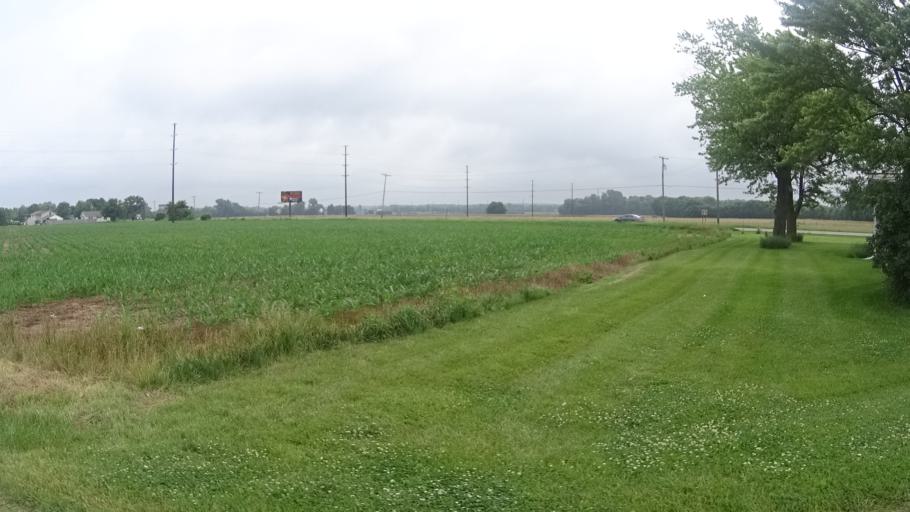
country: US
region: Ohio
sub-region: Erie County
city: Sandusky
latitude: 41.3529
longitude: -82.7541
